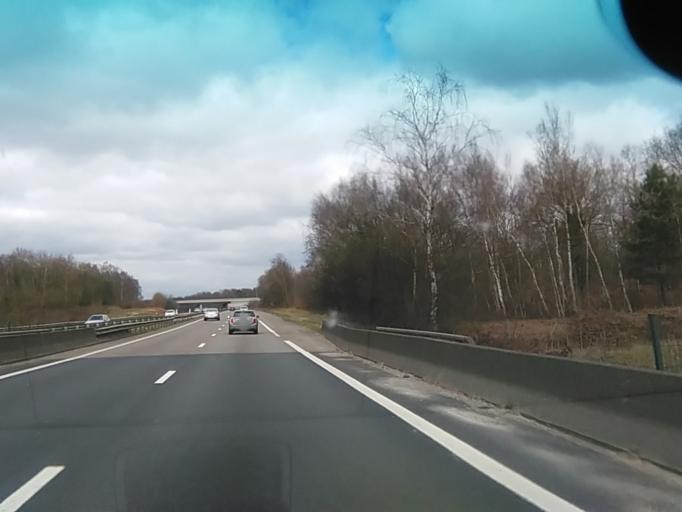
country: FR
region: Haute-Normandie
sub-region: Departement de la Seine-Maritime
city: Le Grand-Quevilly
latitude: 49.3799
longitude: 1.0485
